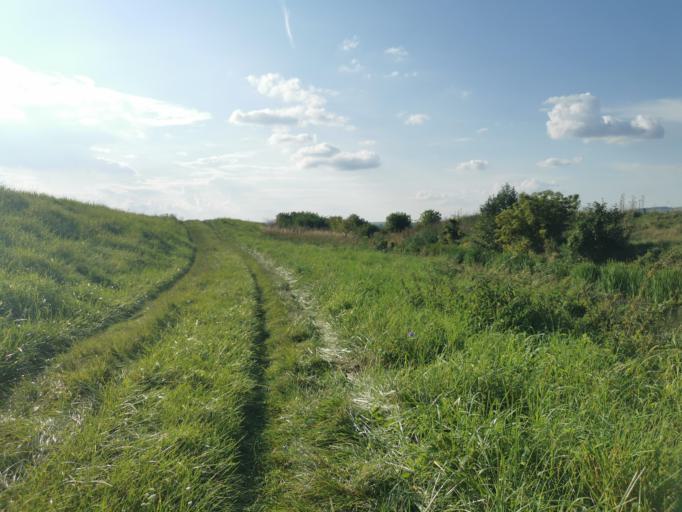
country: SK
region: Trnavsky
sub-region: Okres Senica
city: Senica
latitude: 48.6665
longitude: 17.3017
